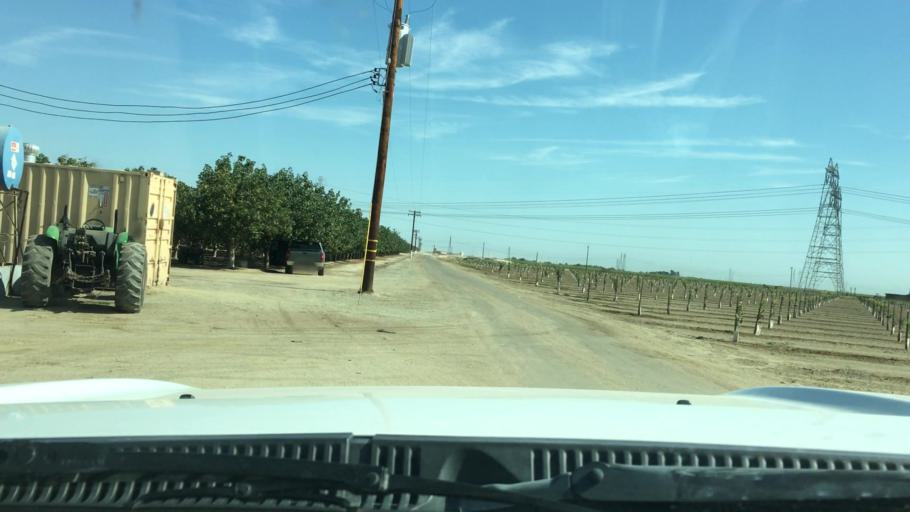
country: US
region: California
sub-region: Kern County
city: Buttonwillow
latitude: 35.3661
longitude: -119.3857
